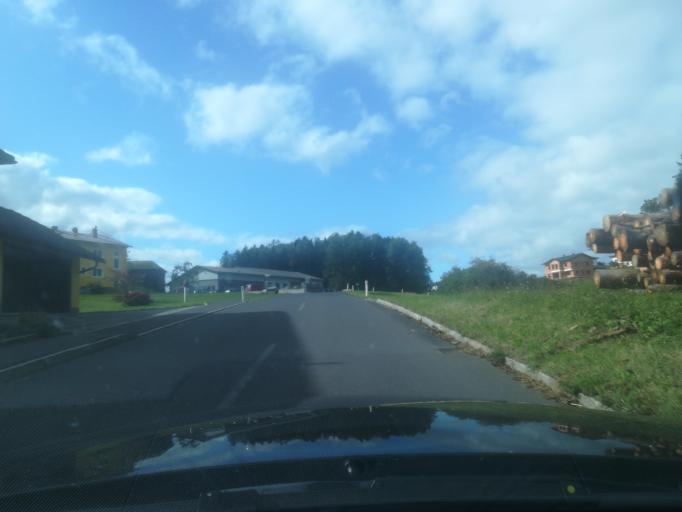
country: AT
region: Upper Austria
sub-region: Politischer Bezirk Urfahr-Umgebung
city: Herzogsdorf
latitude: 48.4302
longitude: 14.1225
